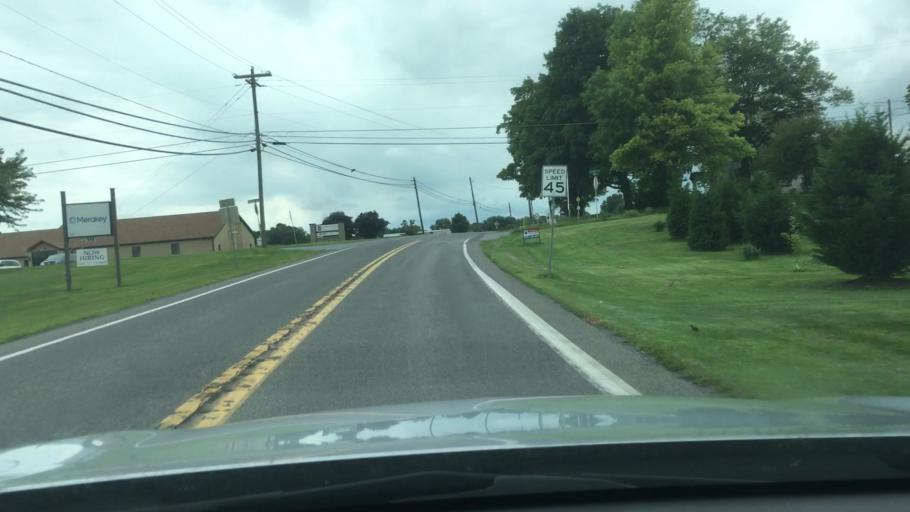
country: US
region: Pennsylvania
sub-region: Franklin County
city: Chambersburg
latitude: 39.9119
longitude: -77.7071
